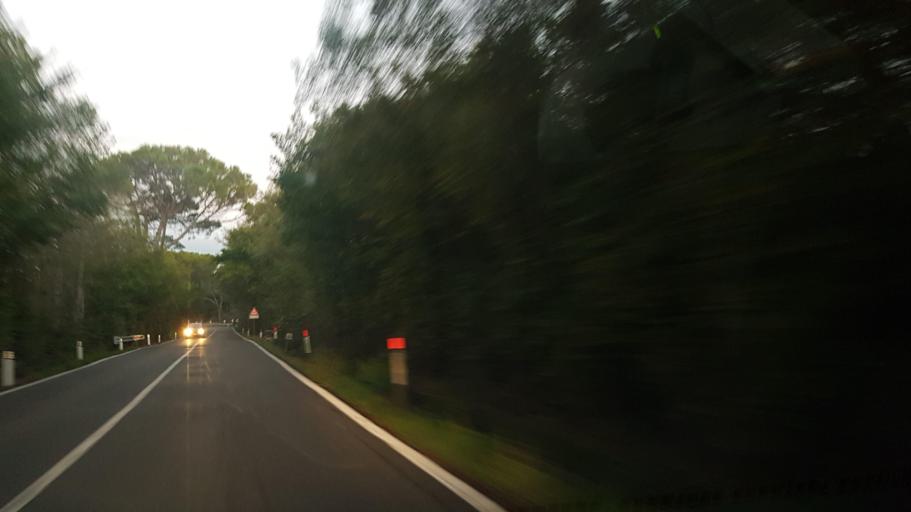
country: IT
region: Basilicate
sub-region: Provincia di Matera
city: Matera
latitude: 40.6768
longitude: 16.6619
